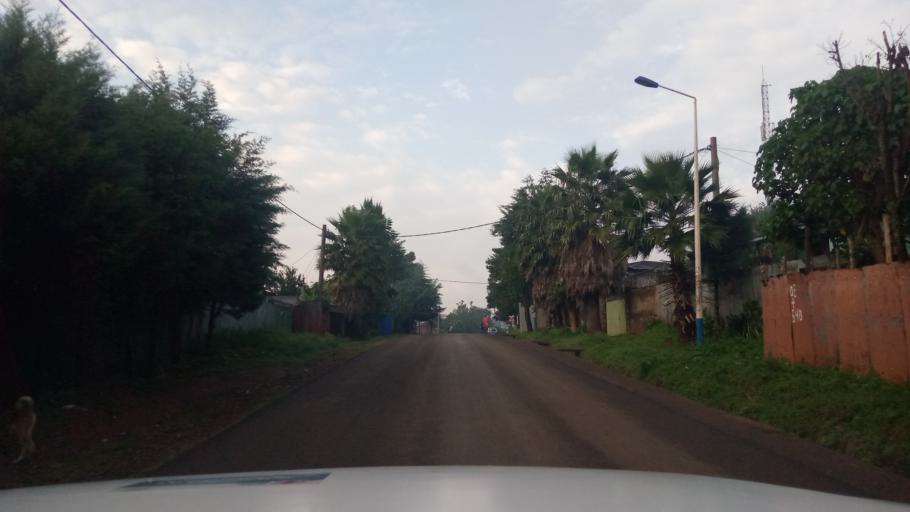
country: ET
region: Oromiya
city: Jima
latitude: 7.6786
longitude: 36.8400
